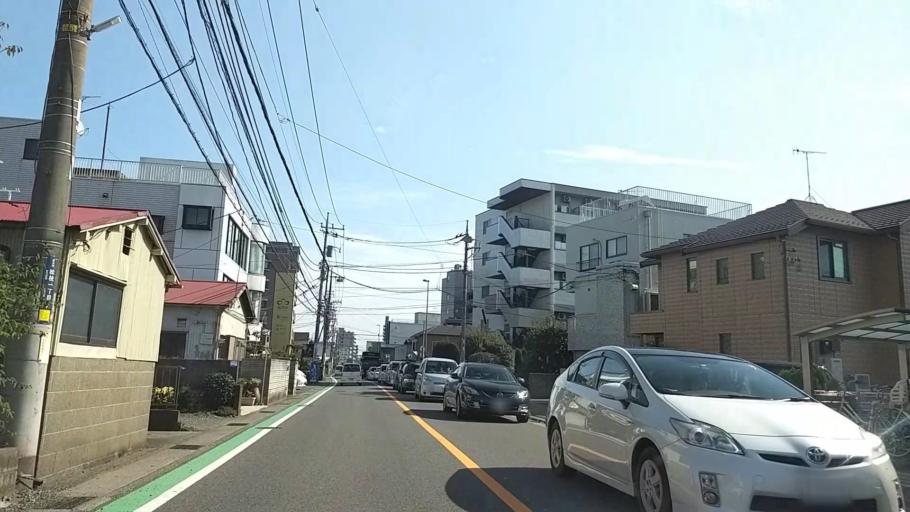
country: JP
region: Kanagawa
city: Atsugi
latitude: 35.4488
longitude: 139.3612
